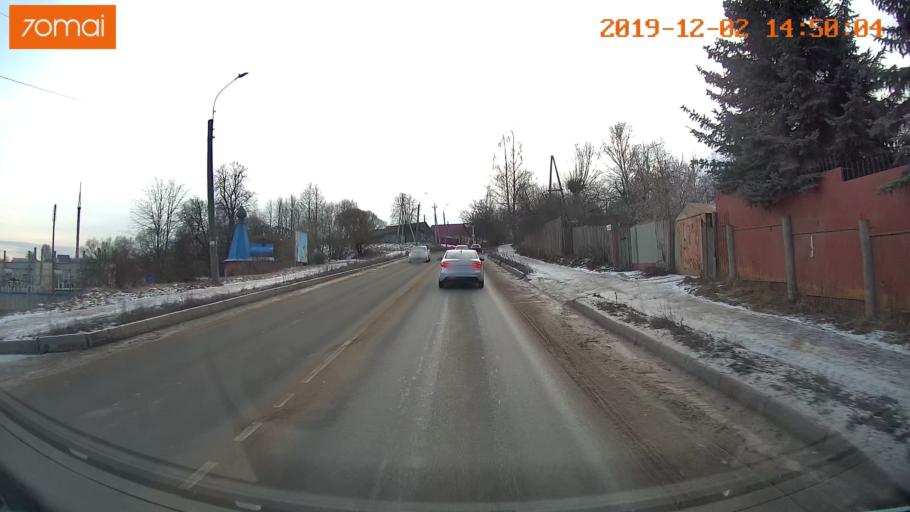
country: RU
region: Ivanovo
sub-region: Gorod Ivanovo
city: Ivanovo
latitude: 56.9825
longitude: 41.0079
